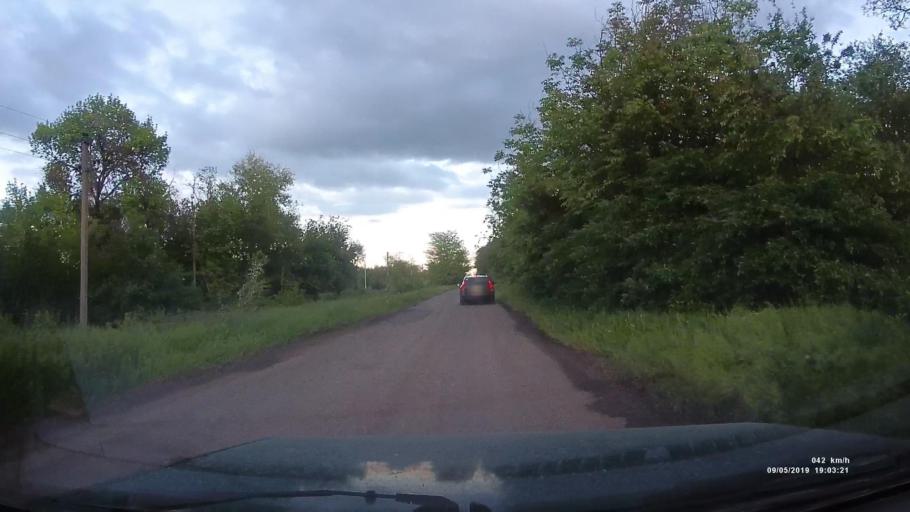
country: RU
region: Krasnodarskiy
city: Kanelovskaya
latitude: 46.7429
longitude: 39.1625
